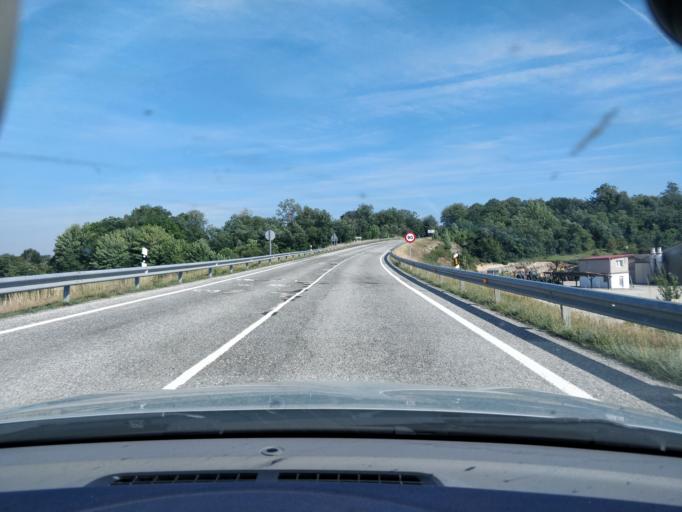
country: ES
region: Cantabria
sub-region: Provincia de Cantabria
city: San Pedro del Romeral
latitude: 42.9662
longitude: -3.7808
